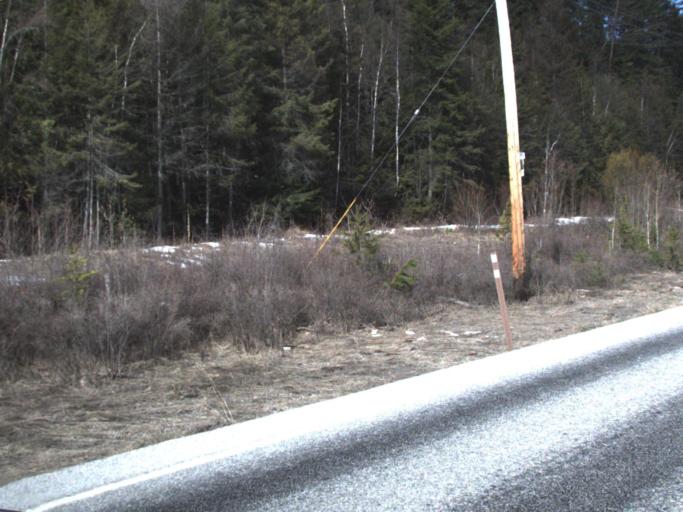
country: US
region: Washington
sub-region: Stevens County
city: Chewelah
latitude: 48.5533
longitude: -117.3426
